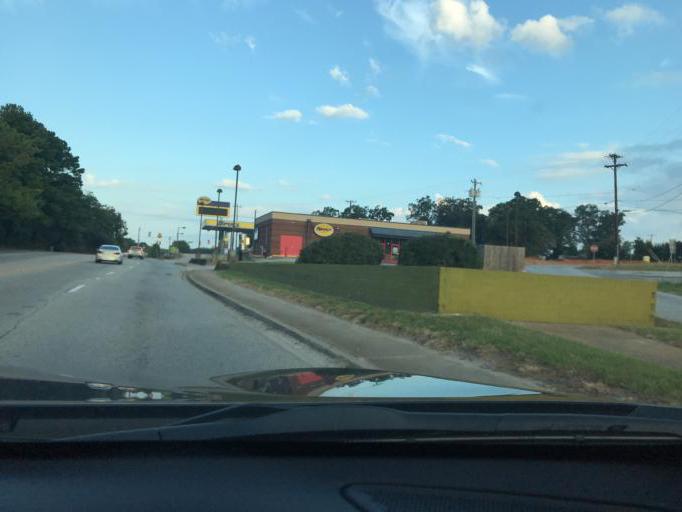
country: US
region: South Carolina
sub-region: Greenville County
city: Dunean
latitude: 34.8189
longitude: -82.4248
